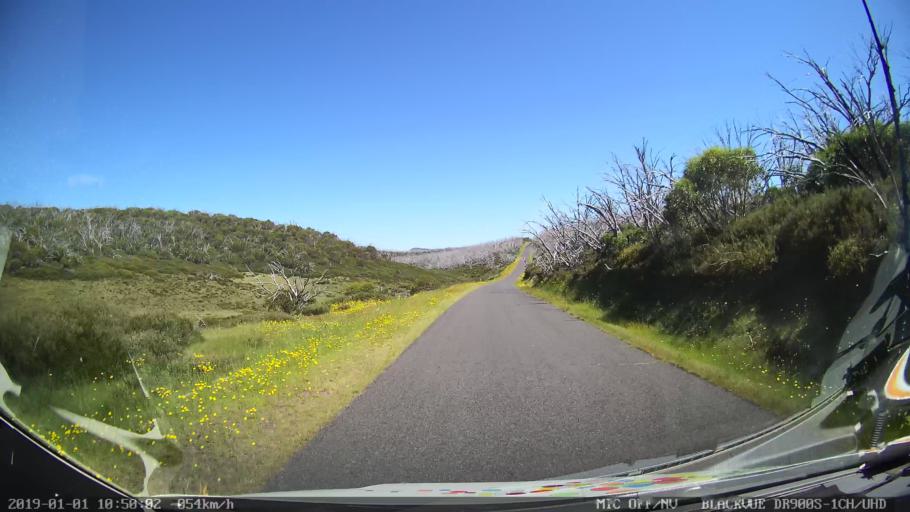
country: AU
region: New South Wales
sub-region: Snowy River
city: Jindabyne
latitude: -36.0319
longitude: 148.3736
